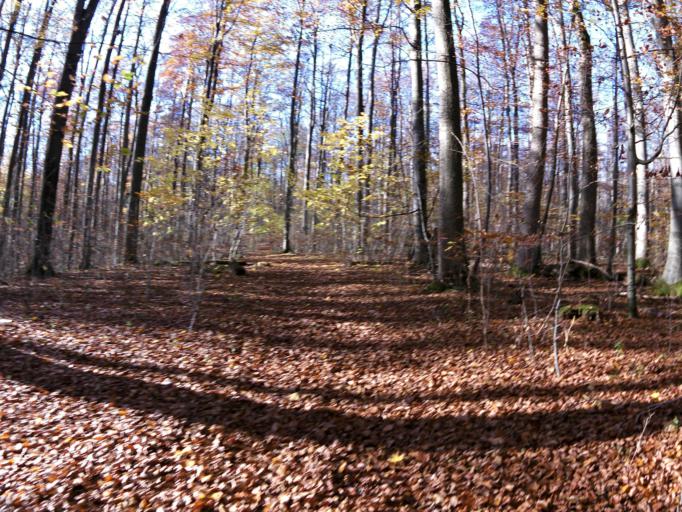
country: DE
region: Thuringia
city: Kammerforst
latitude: 51.0743
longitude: 10.4348
